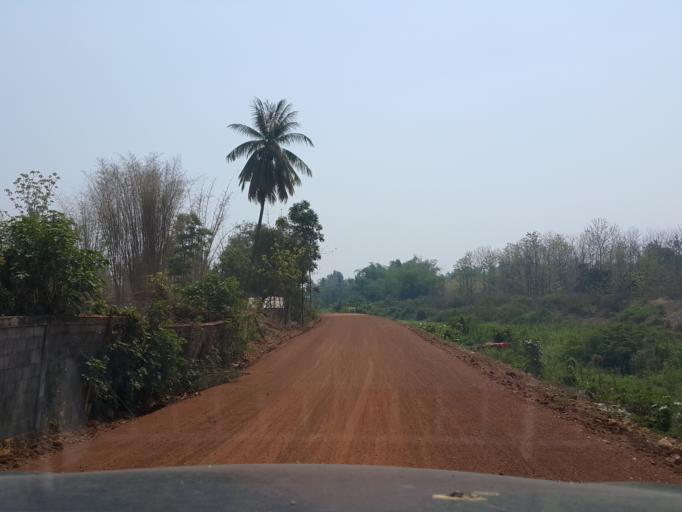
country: TH
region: Sukhothai
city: Thung Saliam
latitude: 17.3142
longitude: 99.5533
